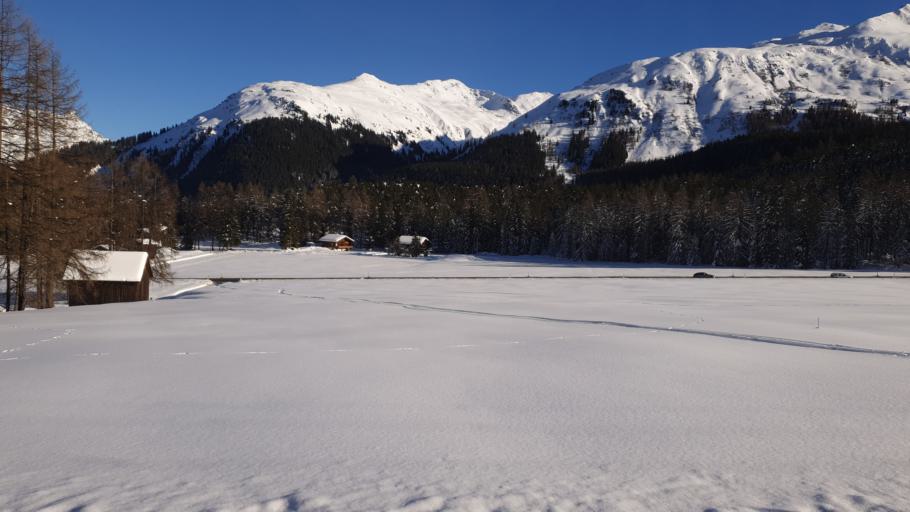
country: CH
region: Grisons
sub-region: Praettigau/Davos District
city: Davos
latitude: 46.8392
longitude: 9.8551
